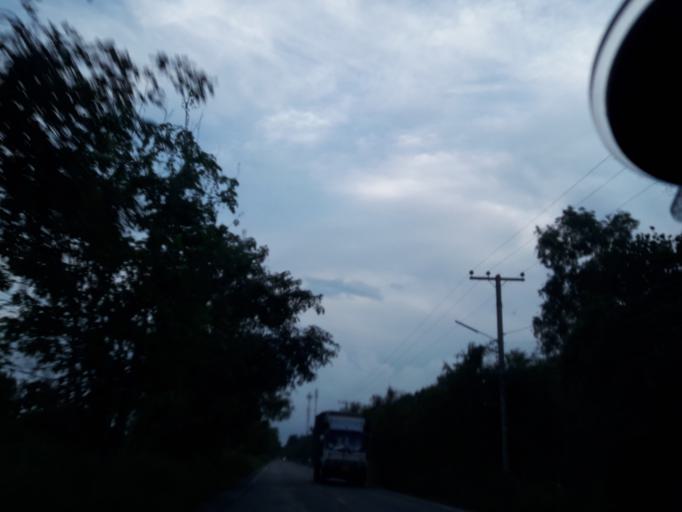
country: TH
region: Pathum Thani
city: Nong Suea
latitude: 14.1123
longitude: 100.8685
